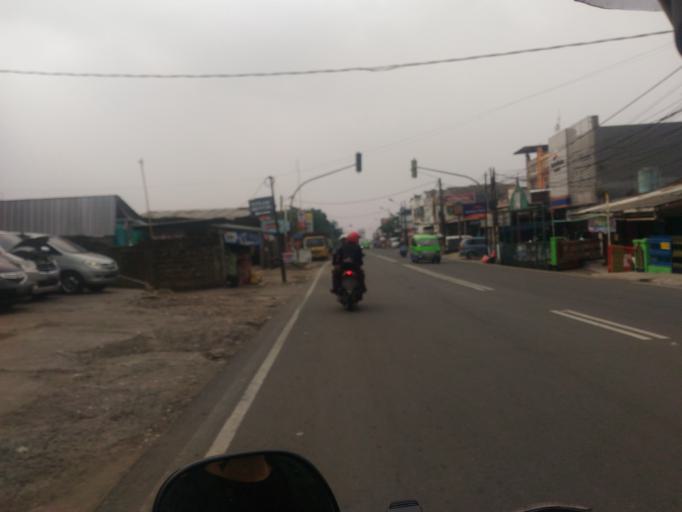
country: ID
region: West Java
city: Caringin
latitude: -6.6536
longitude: 106.8460
